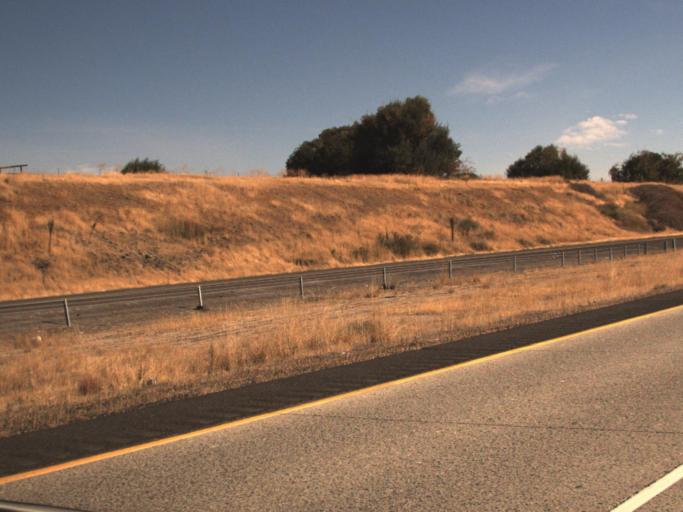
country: US
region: Washington
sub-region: Benton County
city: Prosser
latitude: 46.2284
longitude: -119.8040
